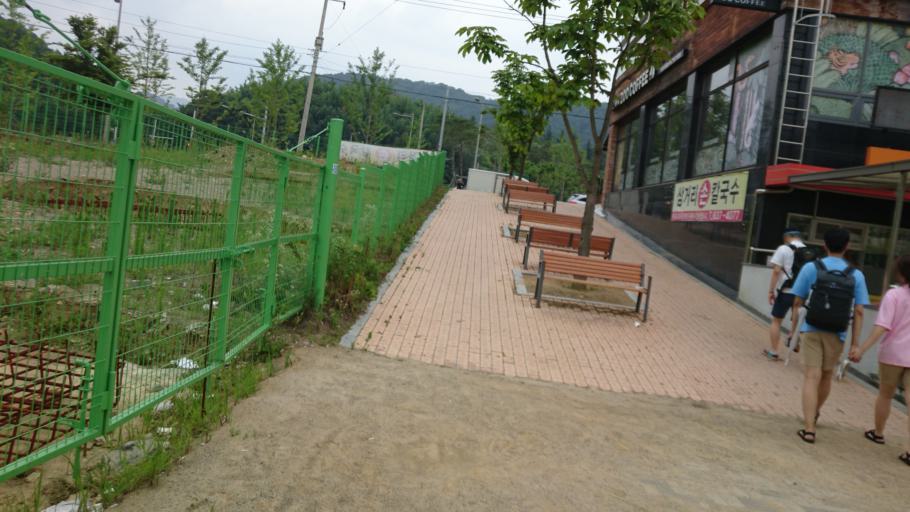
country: KR
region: Daegu
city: Hwawon
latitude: 35.8045
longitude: 128.5198
